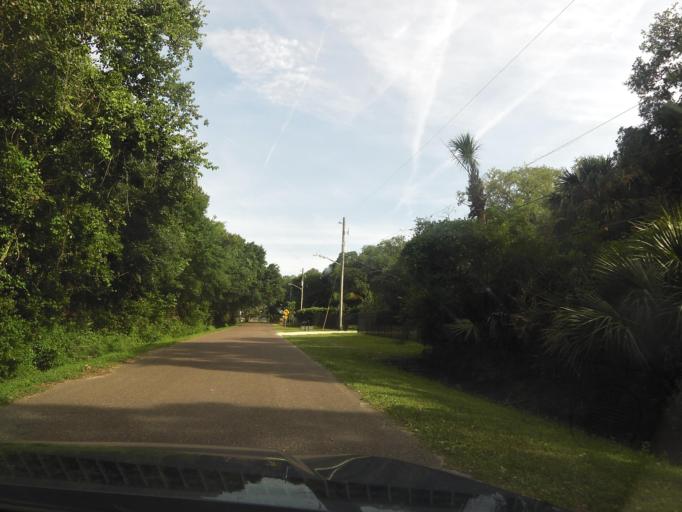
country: US
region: Florida
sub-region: Nassau County
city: Fernandina Beach
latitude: 30.5191
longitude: -81.4912
